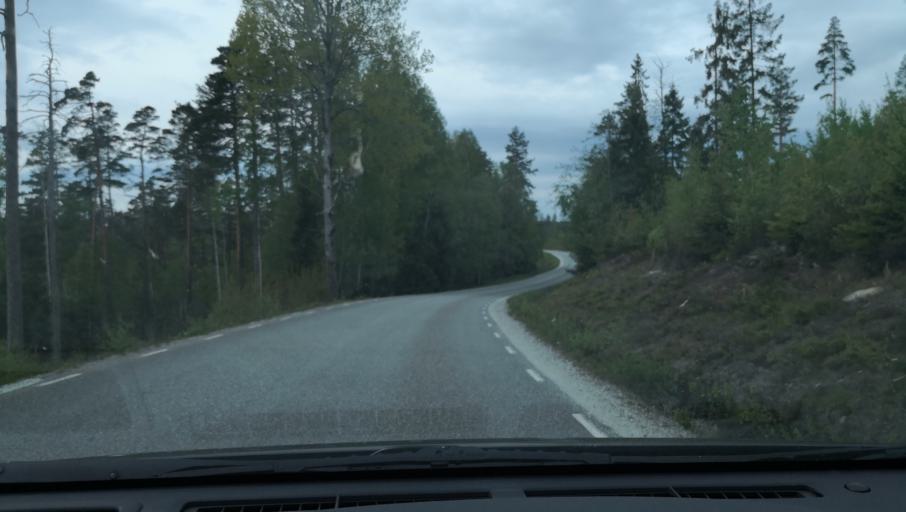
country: SE
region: Vaestmanland
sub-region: Skinnskattebergs Kommun
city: Skinnskatteberg
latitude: 59.8241
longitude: 15.5815
